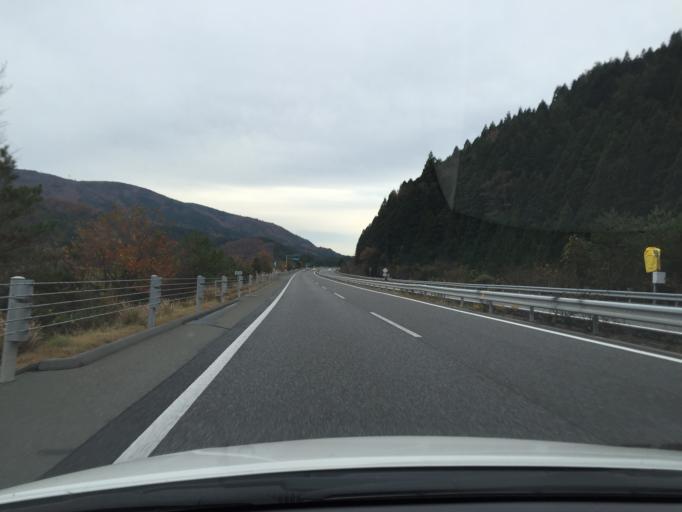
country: JP
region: Fukushima
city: Iwaki
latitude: 37.1089
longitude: 140.7595
